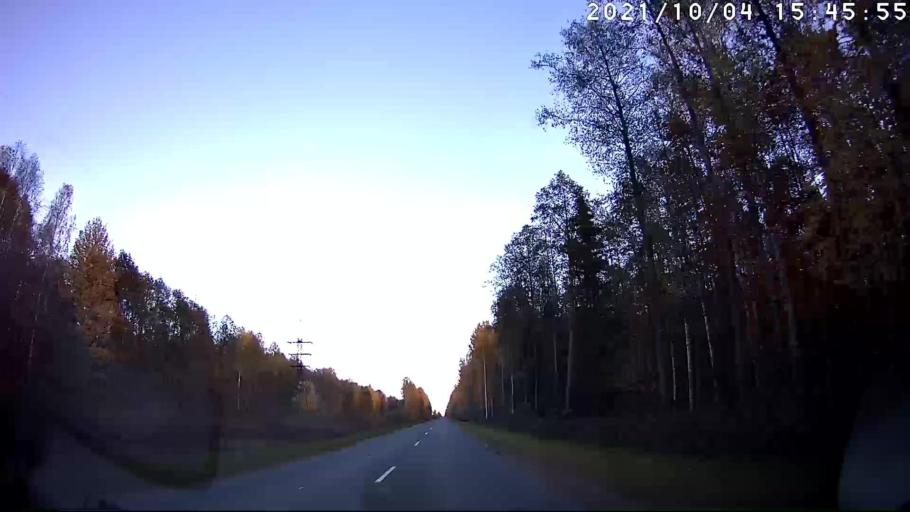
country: RU
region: Mariy-El
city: Surok
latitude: 56.5695
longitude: 48.2398
